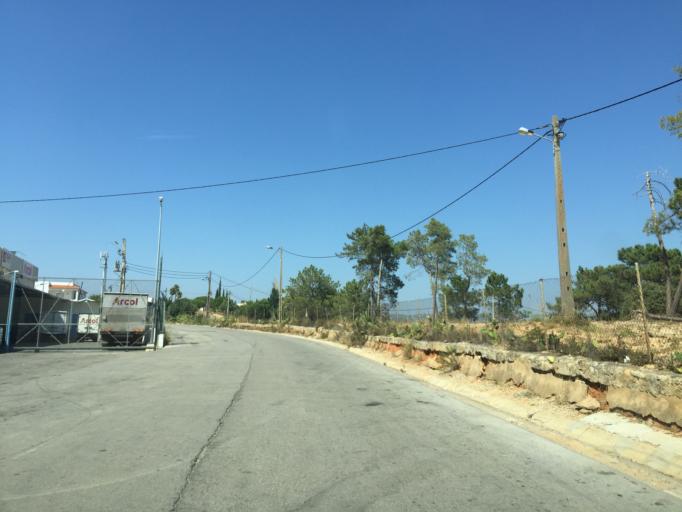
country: PT
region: Faro
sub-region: Faro
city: Faro
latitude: 37.0378
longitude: -7.8962
